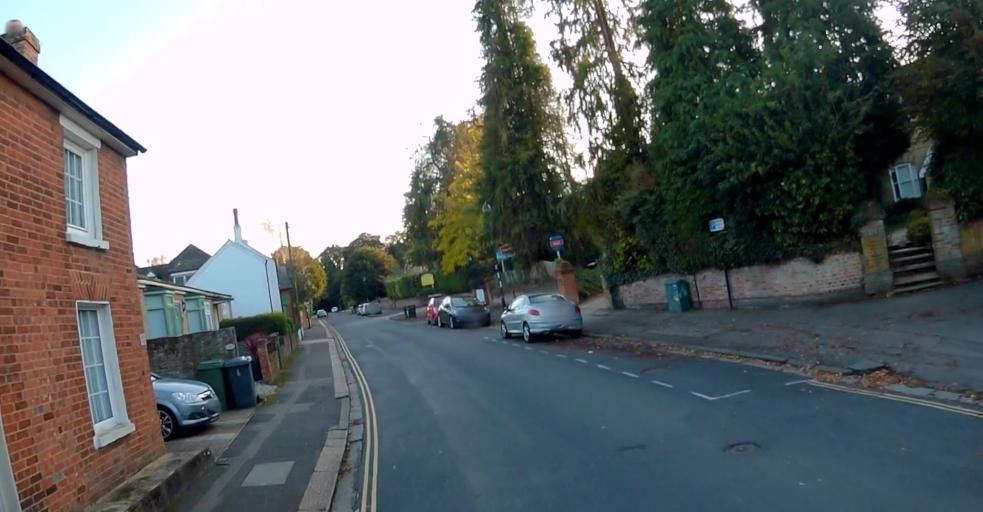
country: GB
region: England
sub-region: Hampshire
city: Basingstoke
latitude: 51.2597
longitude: -1.0845
